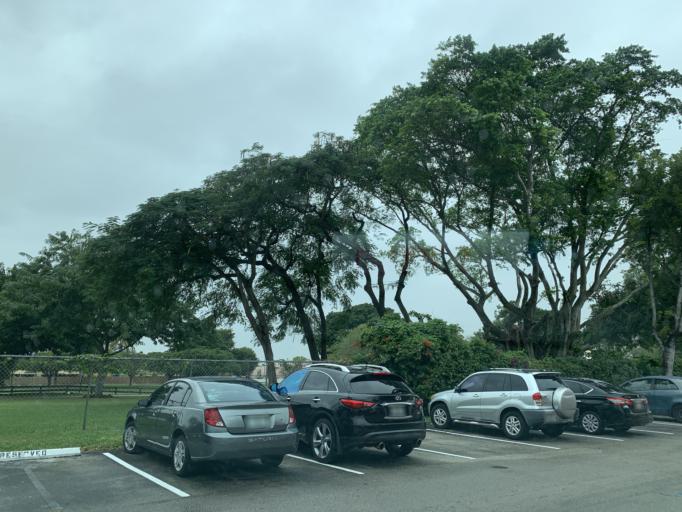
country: US
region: Florida
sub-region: Miami-Dade County
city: Kendall West
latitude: 25.6925
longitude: -80.4355
